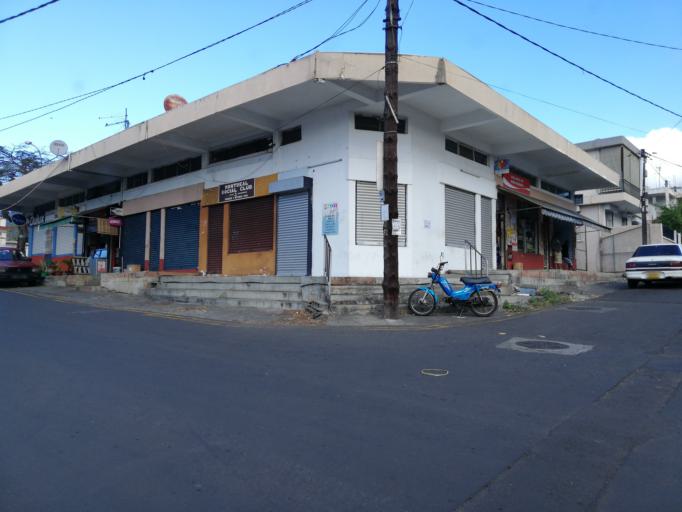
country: MU
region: Moka
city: Pailles
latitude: -20.1994
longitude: 57.4694
